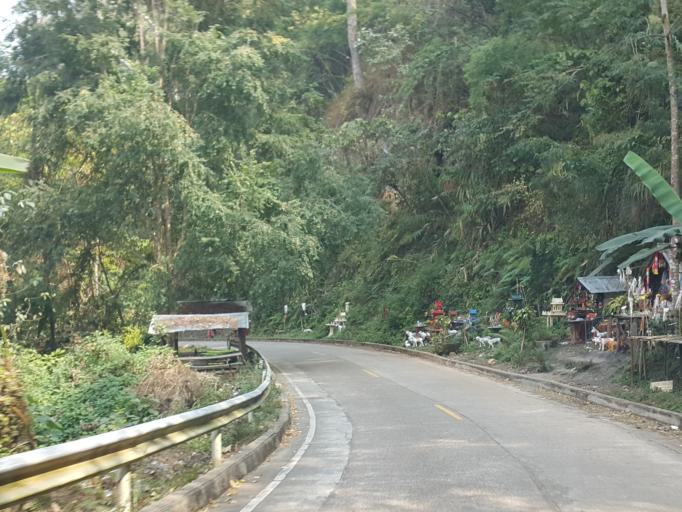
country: TH
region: Chiang Mai
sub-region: Amphoe Chiang Dao
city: Chiang Dao
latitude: 19.4110
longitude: 98.8613
